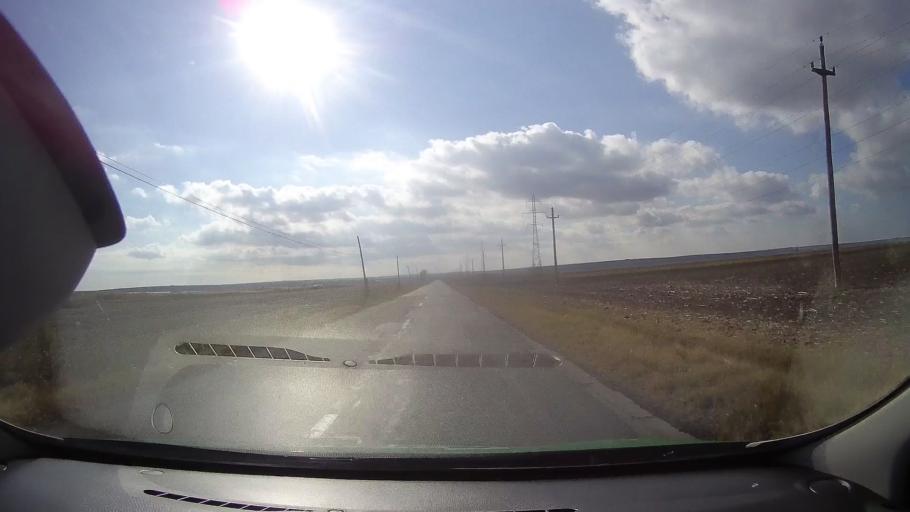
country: RO
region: Constanta
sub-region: Comuna Istria
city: Istria
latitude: 44.5407
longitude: 28.6895
